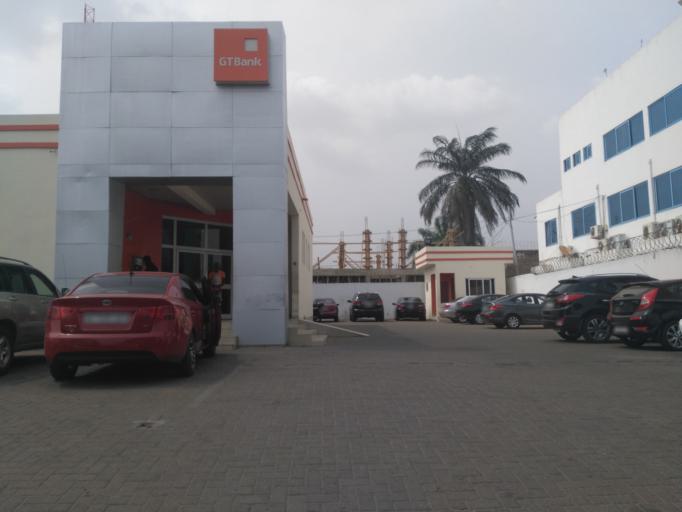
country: GH
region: Greater Accra
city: Accra
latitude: 5.5640
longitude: -0.1817
